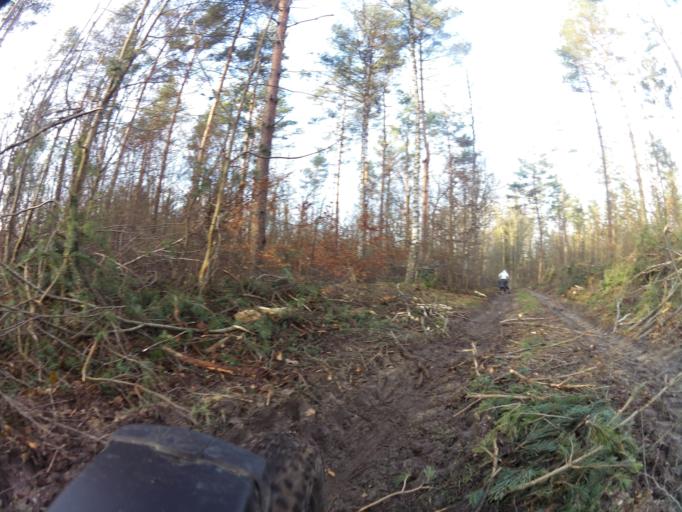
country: PL
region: West Pomeranian Voivodeship
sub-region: Powiat koszalinski
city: Polanow
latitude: 54.0826
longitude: 16.6477
